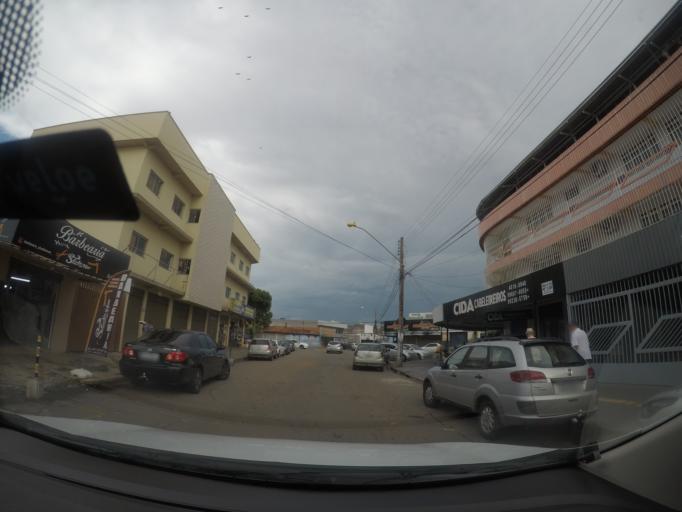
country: BR
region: Goias
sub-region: Goiania
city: Goiania
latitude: -16.6689
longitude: -49.2794
